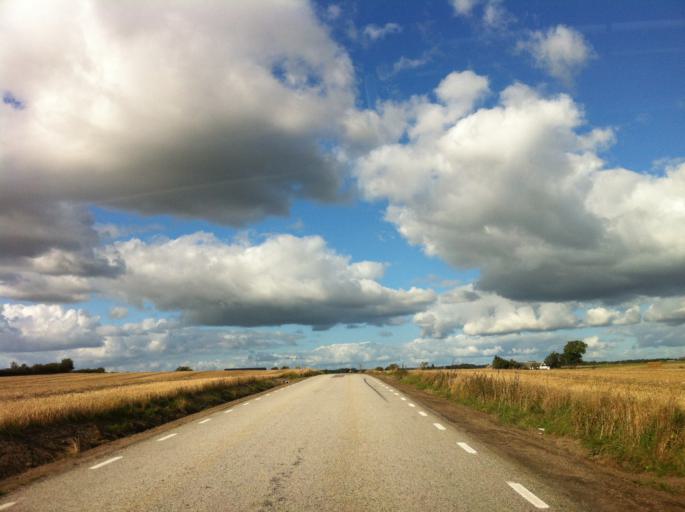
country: SE
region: Skane
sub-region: Sjobo Kommun
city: Sjoebo
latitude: 55.6425
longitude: 13.8168
